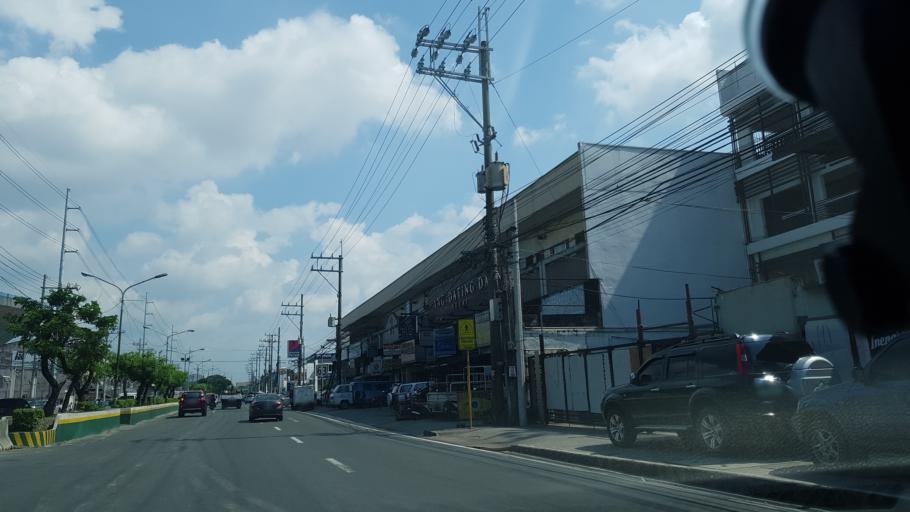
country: PH
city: Sambayanihan People's Village
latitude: 14.4836
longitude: 120.9948
